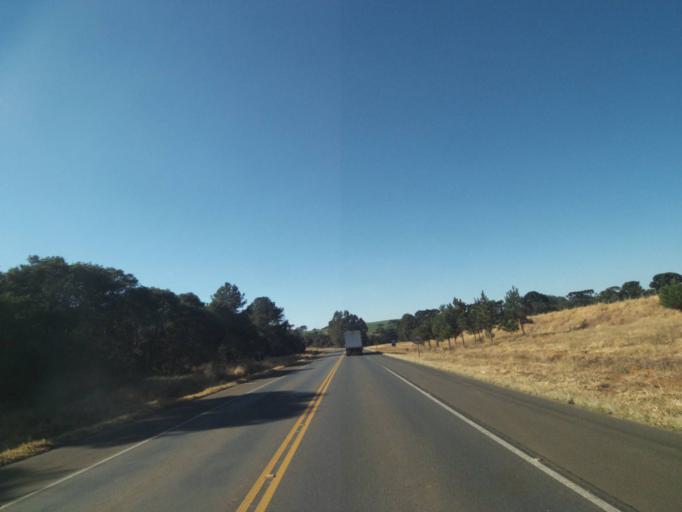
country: BR
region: Parana
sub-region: Tibagi
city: Tibagi
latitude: -24.5504
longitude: -50.4544
